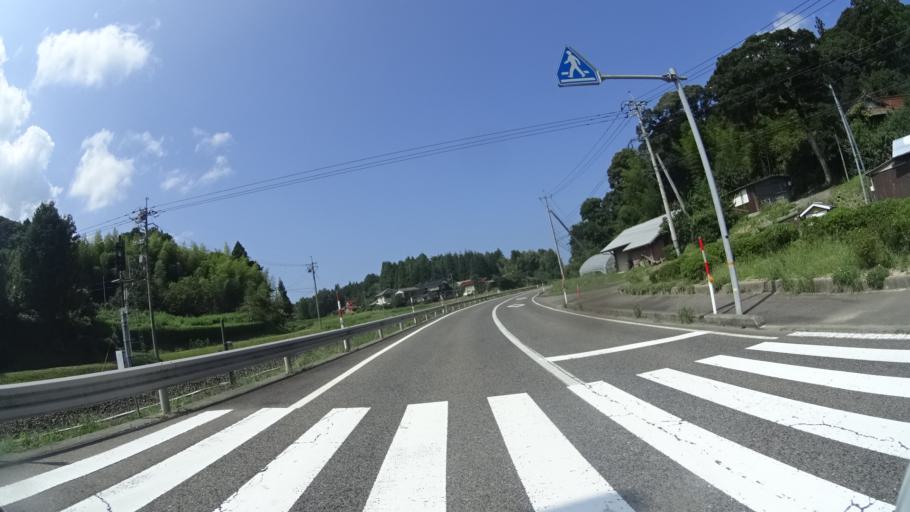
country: JP
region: Shimane
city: Masuda
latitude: 34.6244
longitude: 131.6290
